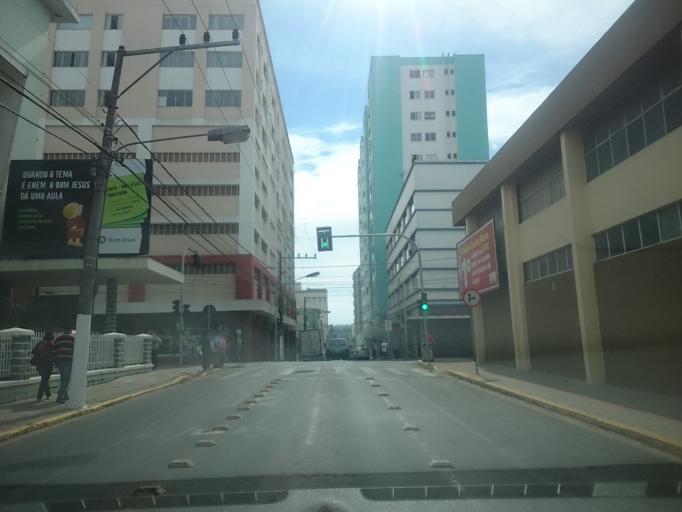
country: BR
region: Santa Catarina
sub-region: Lages
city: Lages
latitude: -27.8182
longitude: -50.3262
